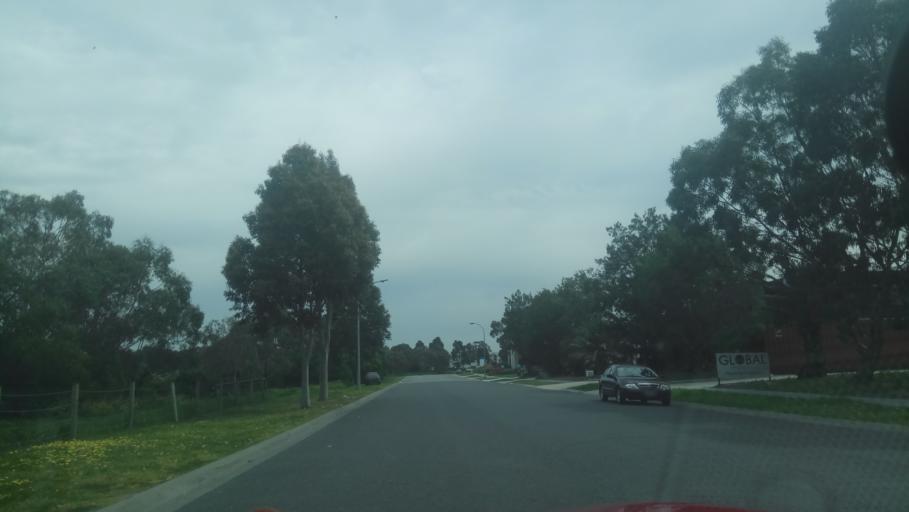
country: AU
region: Victoria
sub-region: Kingston
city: Waterways
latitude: -38.0044
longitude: 145.1186
